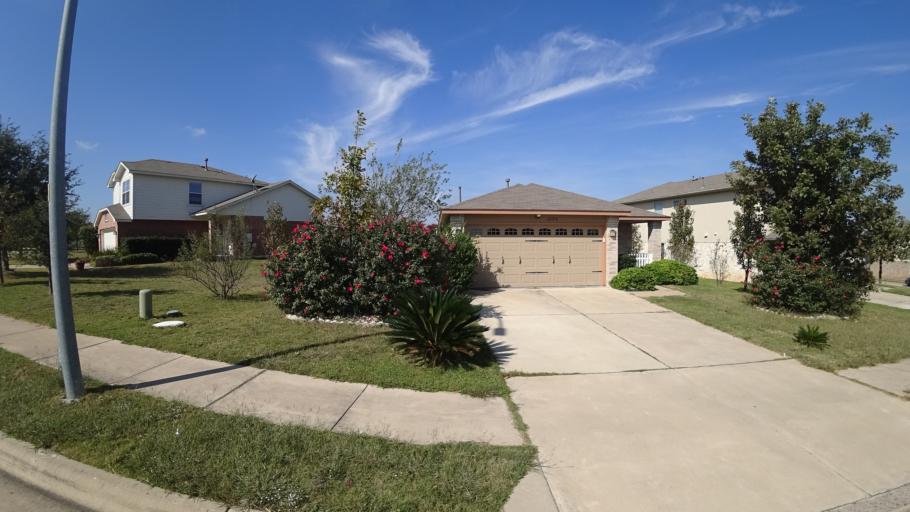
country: US
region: Texas
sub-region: Travis County
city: Pflugerville
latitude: 30.4213
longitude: -97.6326
